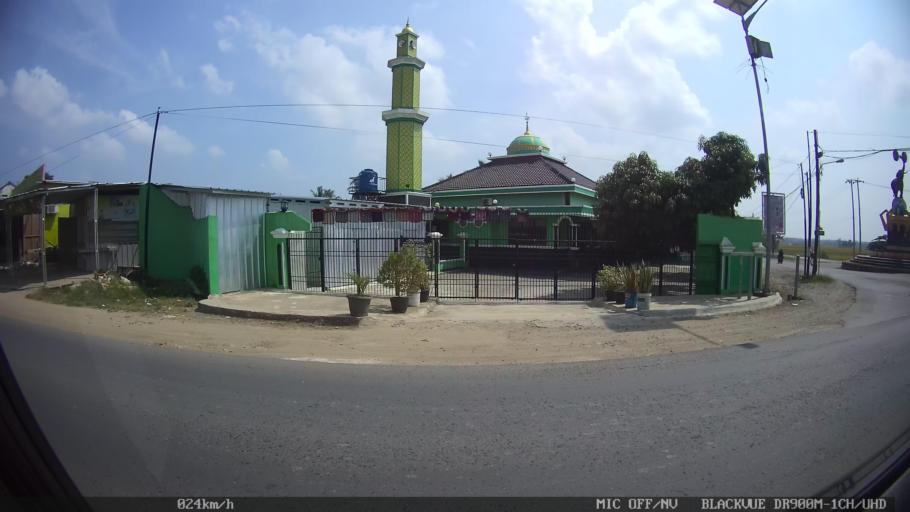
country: ID
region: Lampung
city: Pringsewu
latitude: -5.3636
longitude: 105.0039
